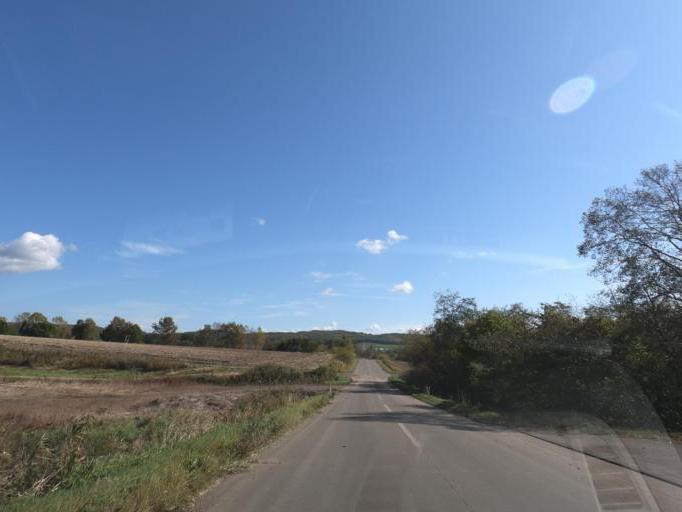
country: JP
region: Hokkaido
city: Otofuke
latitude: 43.0600
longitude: 143.2717
